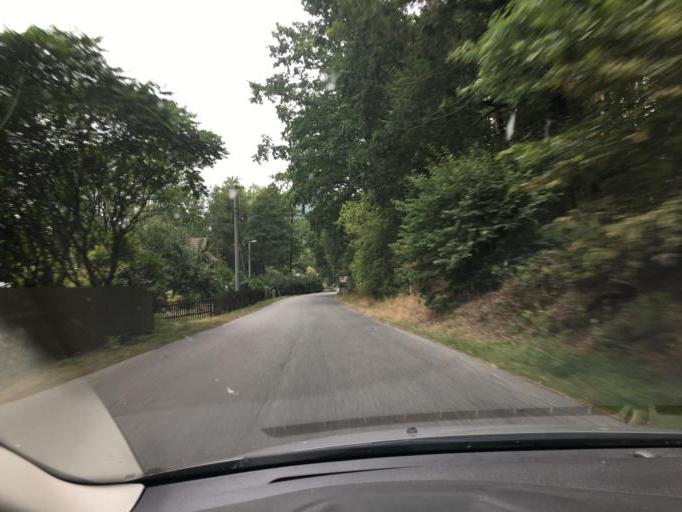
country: CZ
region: Ustecky
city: Ceska Kamenice
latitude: 50.8123
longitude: 14.3549
